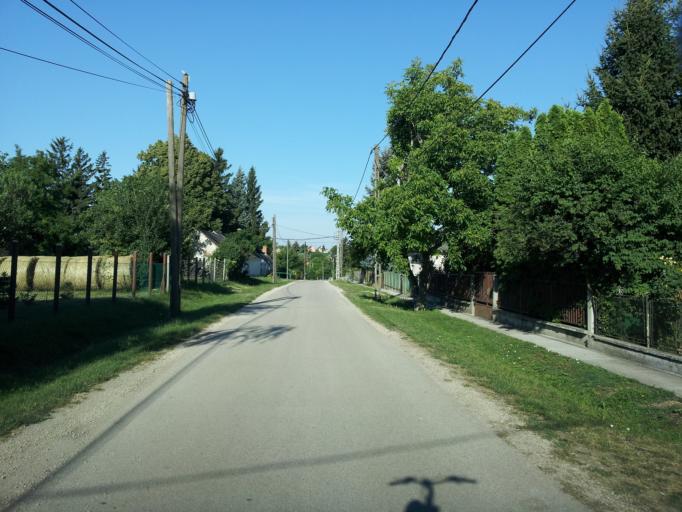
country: HU
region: Fejer
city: Polgardi
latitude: 47.1057
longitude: 18.2547
